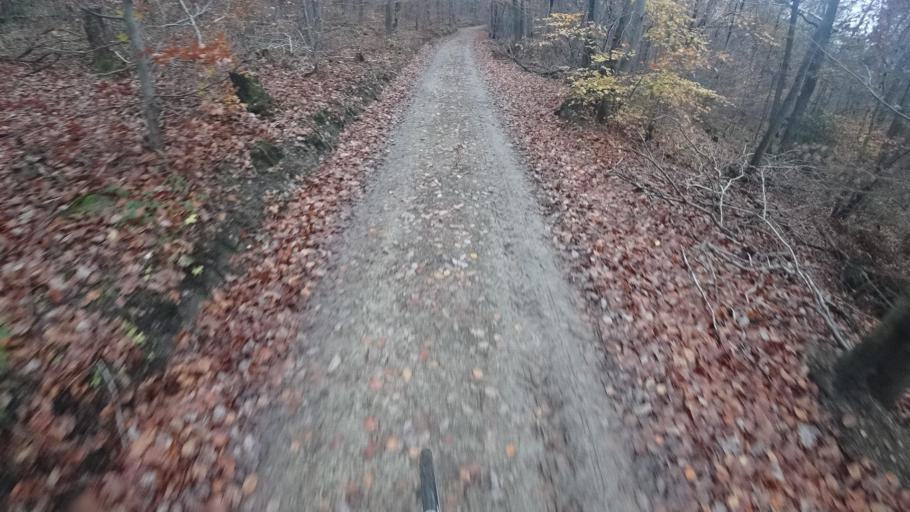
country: DE
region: Rheinland-Pfalz
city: Rech
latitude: 50.5098
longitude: 7.0525
